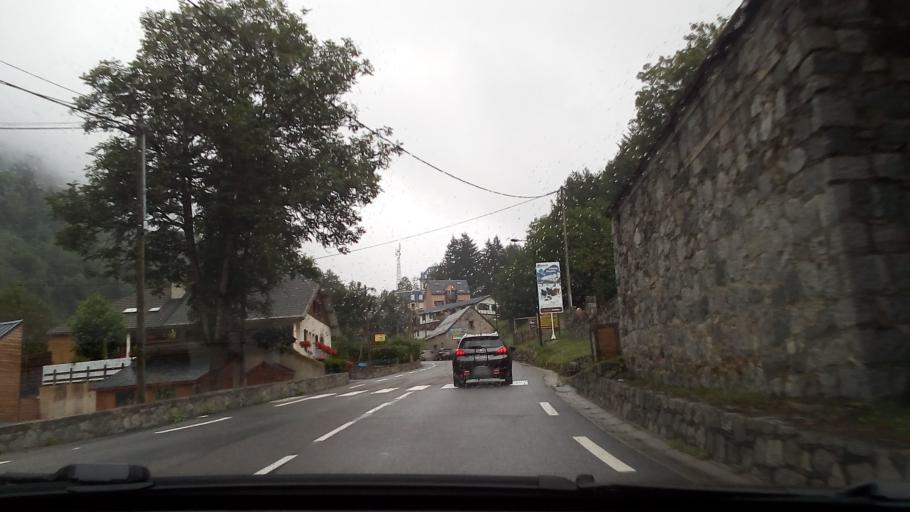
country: FR
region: Midi-Pyrenees
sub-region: Departement des Hautes-Pyrenees
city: Luz-Saint-Sauveur
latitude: 42.8941
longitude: 0.0563
